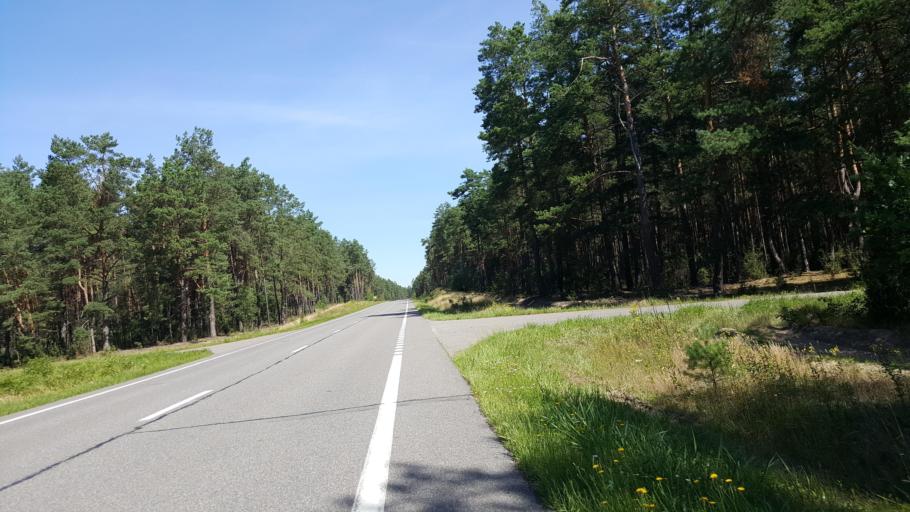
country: BY
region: Brest
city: Zhabinka
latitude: 52.4310
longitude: 24.1257
